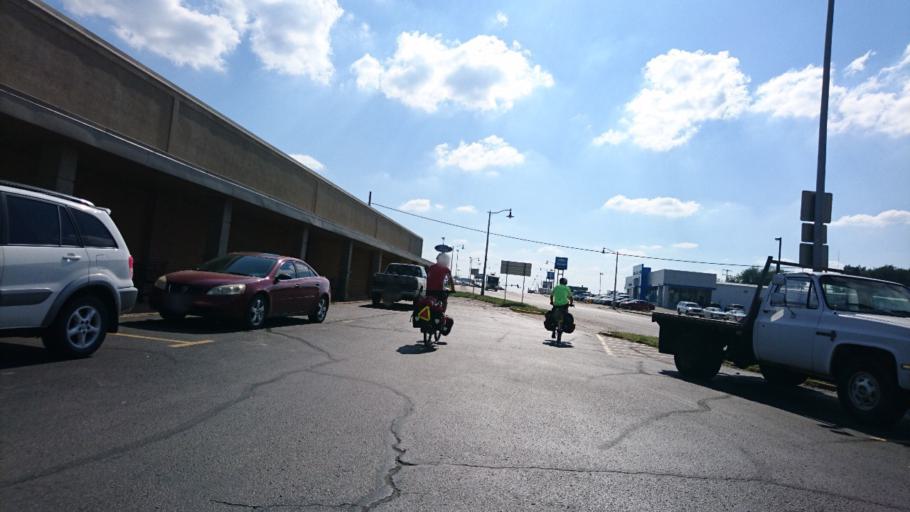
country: US
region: Missouri
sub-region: Laclede County
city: Lebanon
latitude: 37.6759
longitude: -92.6586
